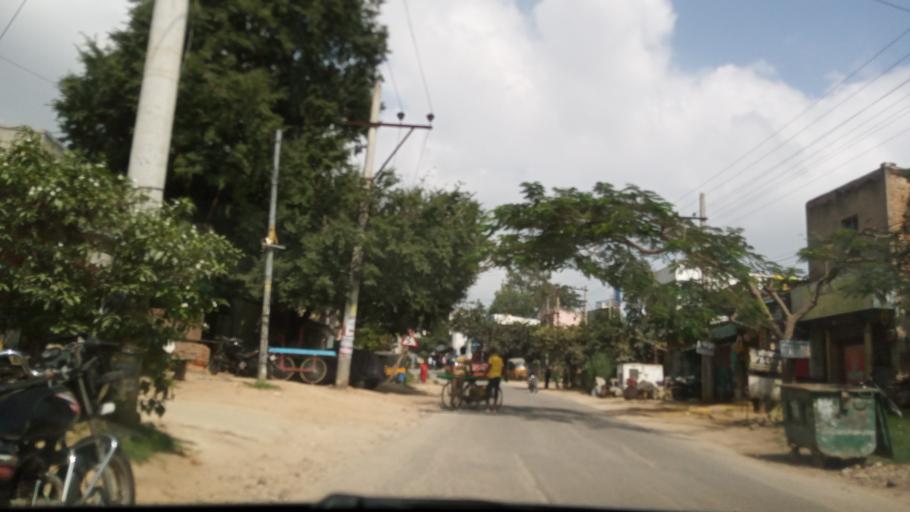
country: IN
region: Andhra Pradesh
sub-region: Chittoor
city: Madanapalle
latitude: 13.5650
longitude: 78.5126
